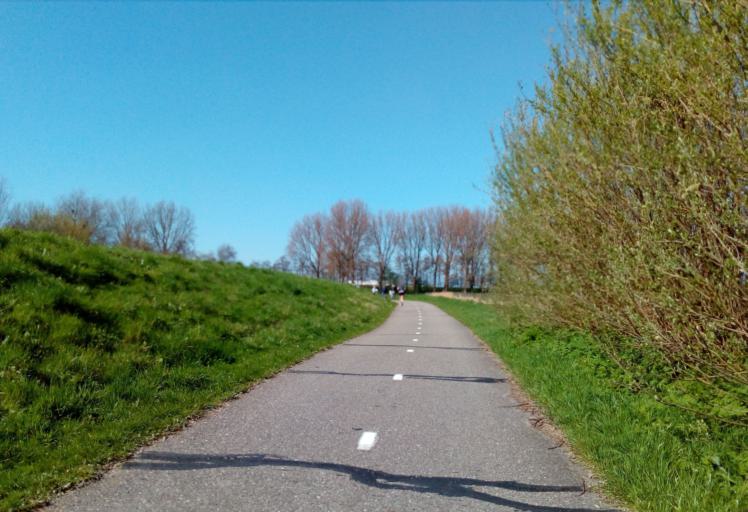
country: NL
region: South Holland
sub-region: Gemeente Westland
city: Kwintsheul
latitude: 51.9877
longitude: 4.2903
